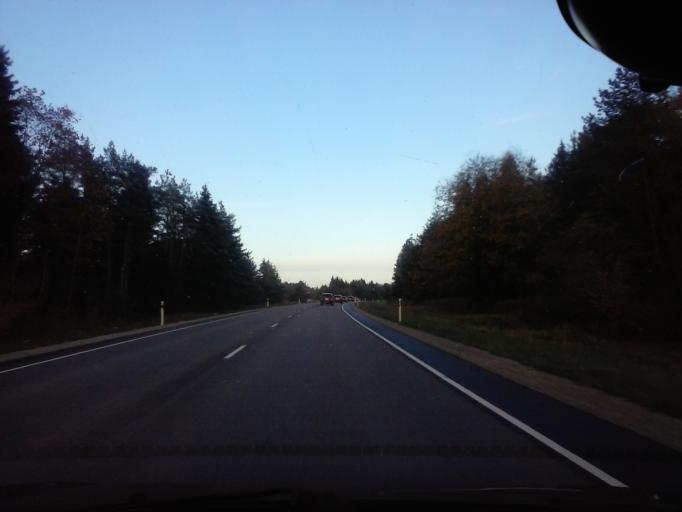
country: EE
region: Harju
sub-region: Nissi vald
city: Turba
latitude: 58.9923
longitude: 24.0260
